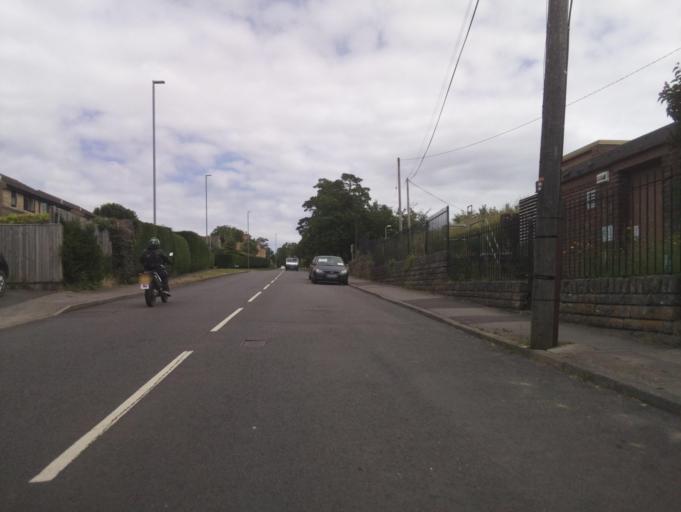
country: GB
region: England
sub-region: Dorset
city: Sherborne
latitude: 50.9571
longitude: -2.5175
